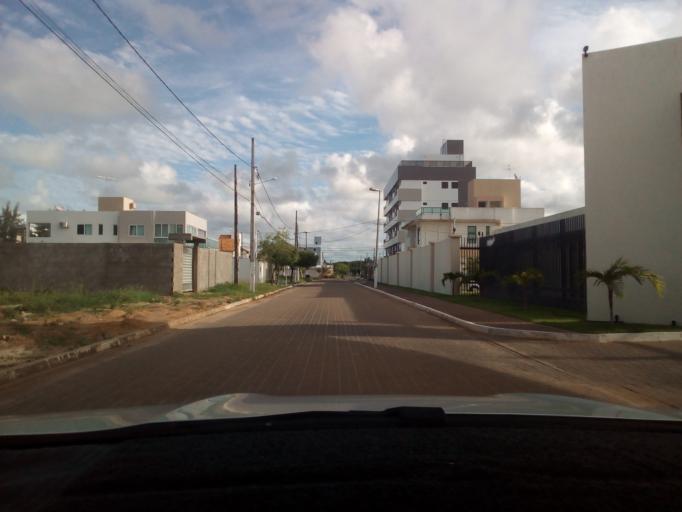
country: BR
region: Paraiba
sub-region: Joao Pessoa
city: Joao Pessoa
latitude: -7.0508
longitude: -34.8456
